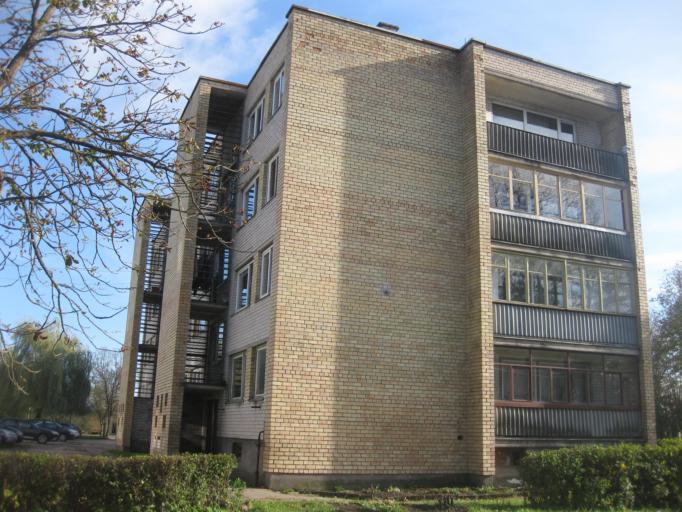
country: LT
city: Ezerelis
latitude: 54.8821
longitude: 23.6043
